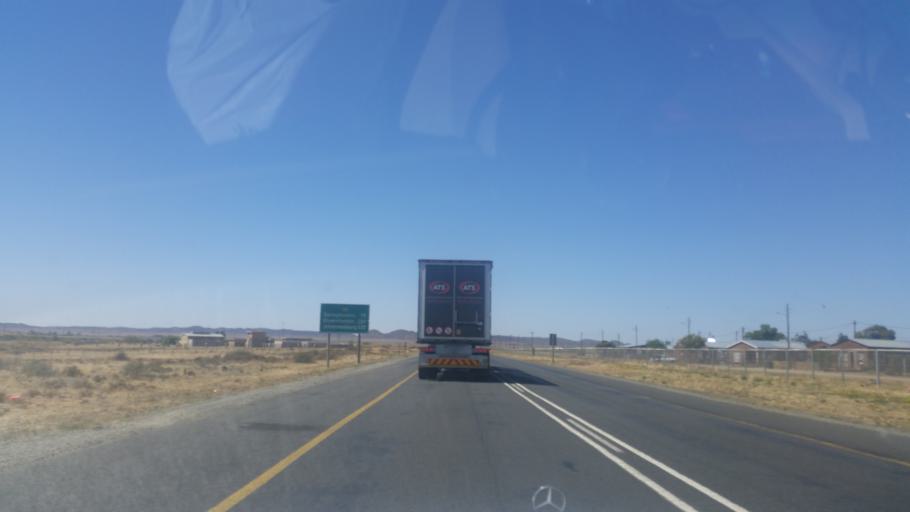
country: ZA
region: Northern Cape
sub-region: Pixley ka Seme District Municipality
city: Colesberg
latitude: -30.7068
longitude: 25.1116
